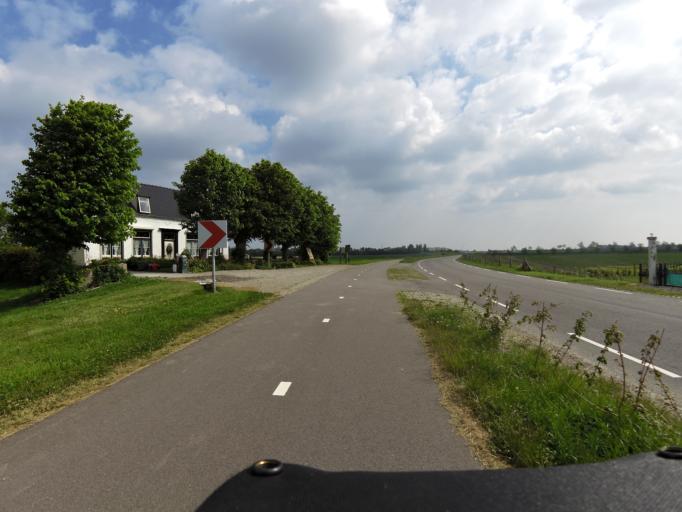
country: NL
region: Zeeland
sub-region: Gemeente Noord-Beveland
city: Kamperland
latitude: 51.5832
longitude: 3.7210
